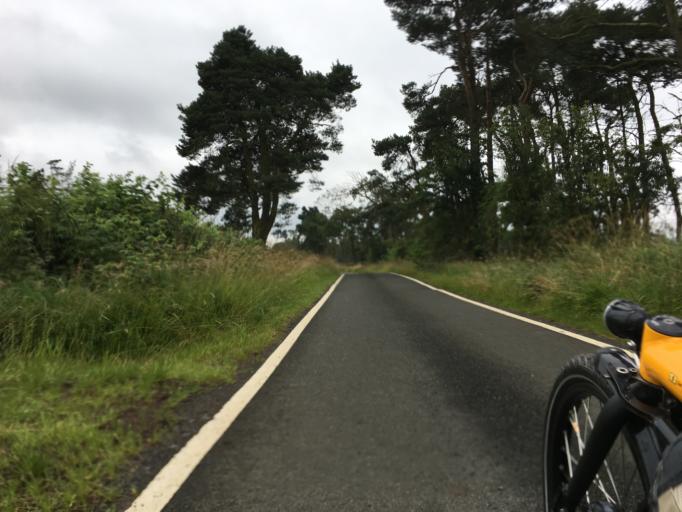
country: GB
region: Scotland
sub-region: West Lothian
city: West Calder
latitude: 55.8468
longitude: -3.5321
